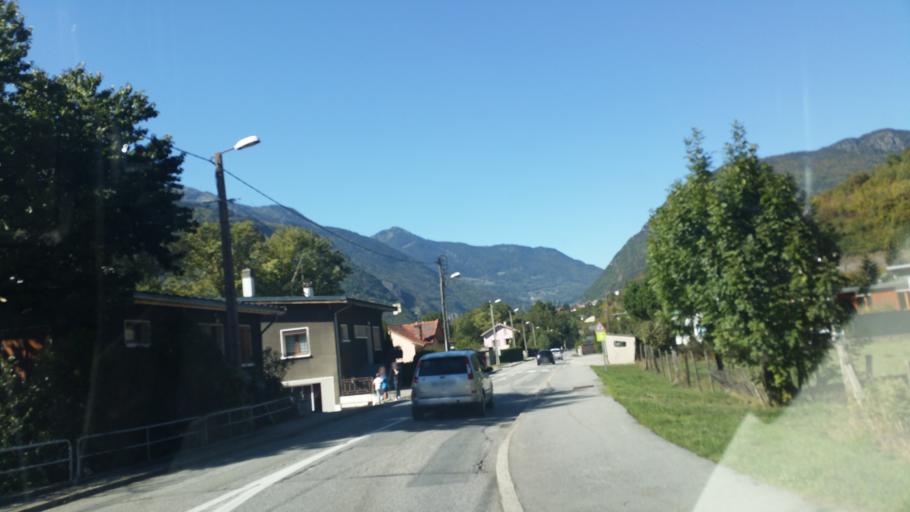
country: FR
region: Rhone-Alpes
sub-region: Departement de la Savoie
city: Aigueblanche
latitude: 45.5058
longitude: 6.5046
